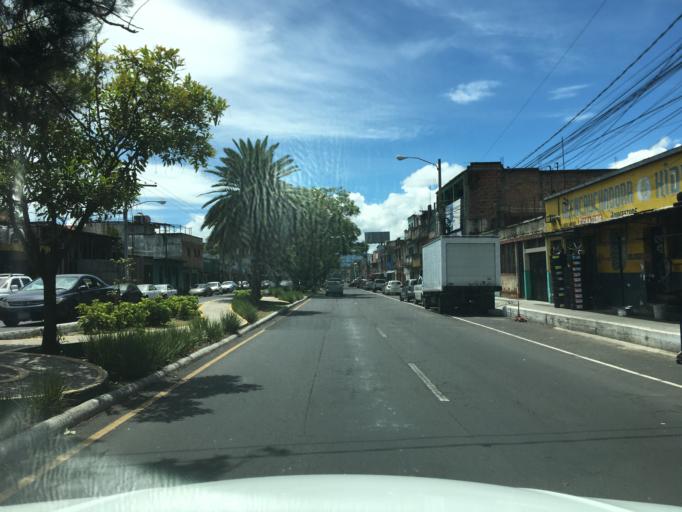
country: GT
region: Guatemala
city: Guatemala City
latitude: 14.6276
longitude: -90.5443
